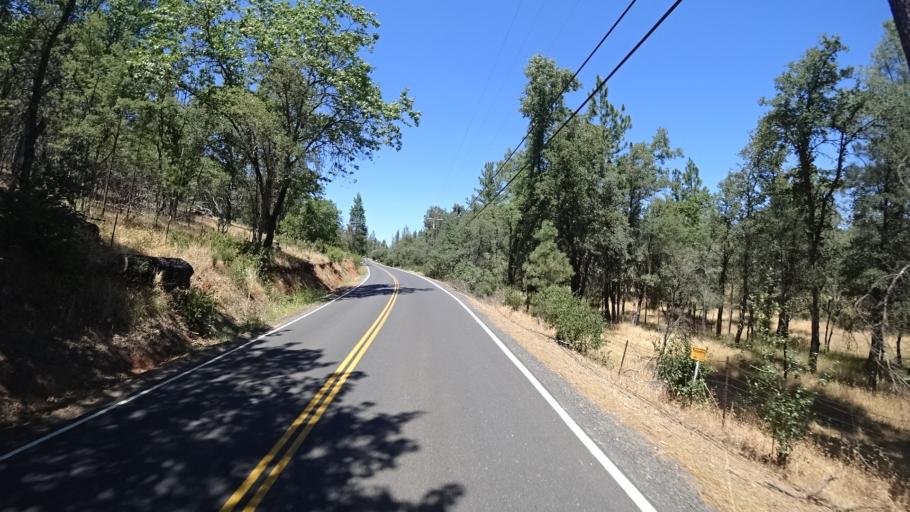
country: US
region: California
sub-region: Calaveras County
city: Mountain Ranch
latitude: 38.2463
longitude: -120.5178
